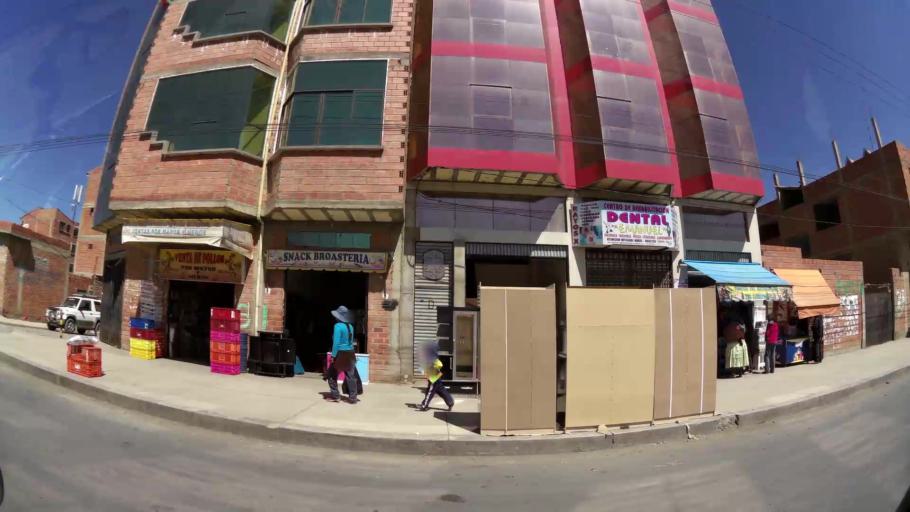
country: BO
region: La Paz
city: La Paz
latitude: -16.5418
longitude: -68.1994
